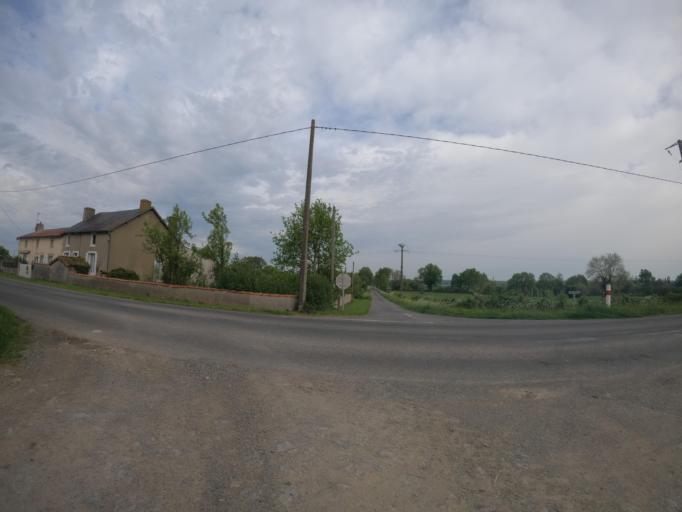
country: FR
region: Poitou-Charentes
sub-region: Departement des Deux-Sevres
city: La Chapelle-Saint-Laurent
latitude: 46.7064
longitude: -0.4814
